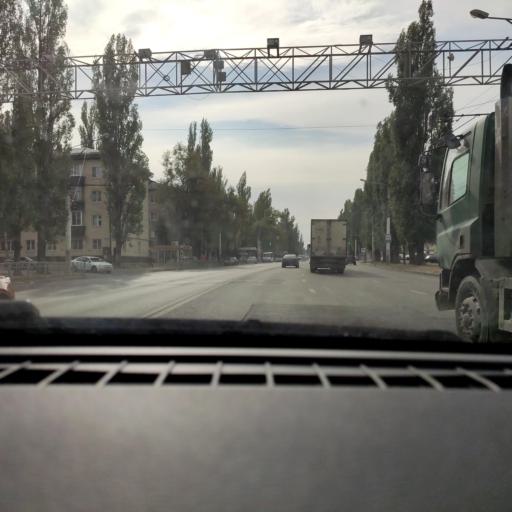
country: RU
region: Voronezj
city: Maslovka
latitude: 51.6177
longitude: 39.2371
